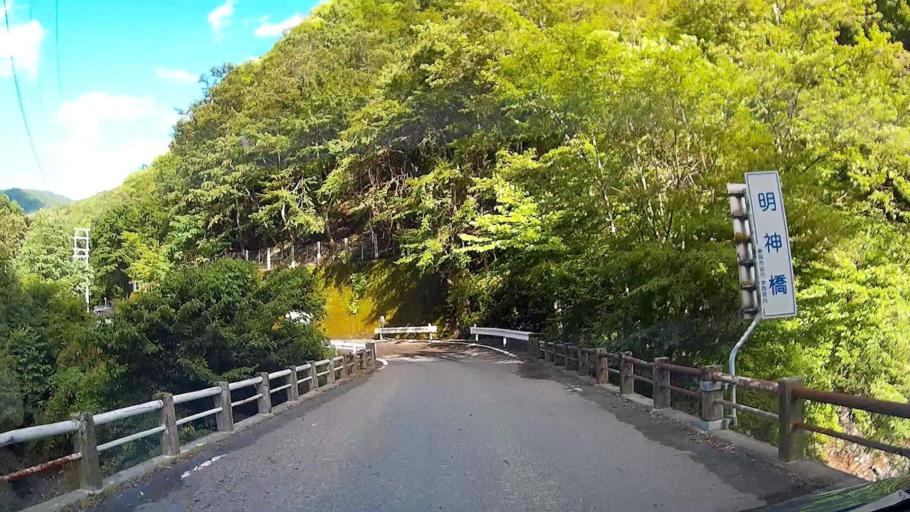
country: JP
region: Shizuoka
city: Shizuoka-shi
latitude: 35.3009
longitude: 138.2047
